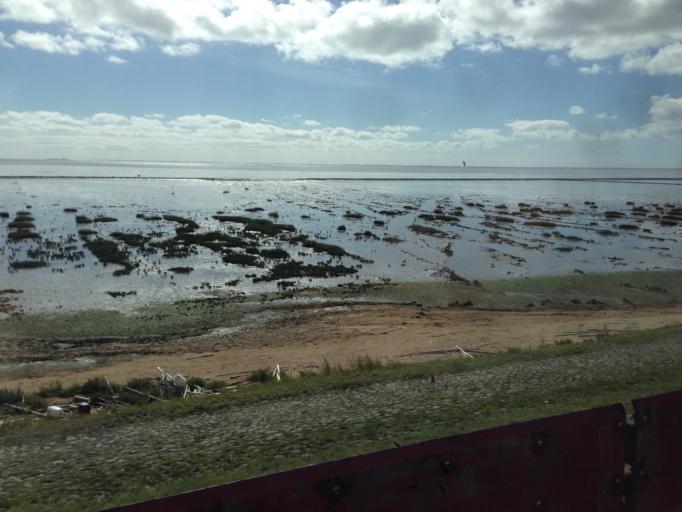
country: DE
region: Schleswig-Holstein
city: Friedrich-Wilhelm-Lubke-Koog
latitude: 54.8854
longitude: 8.5763
